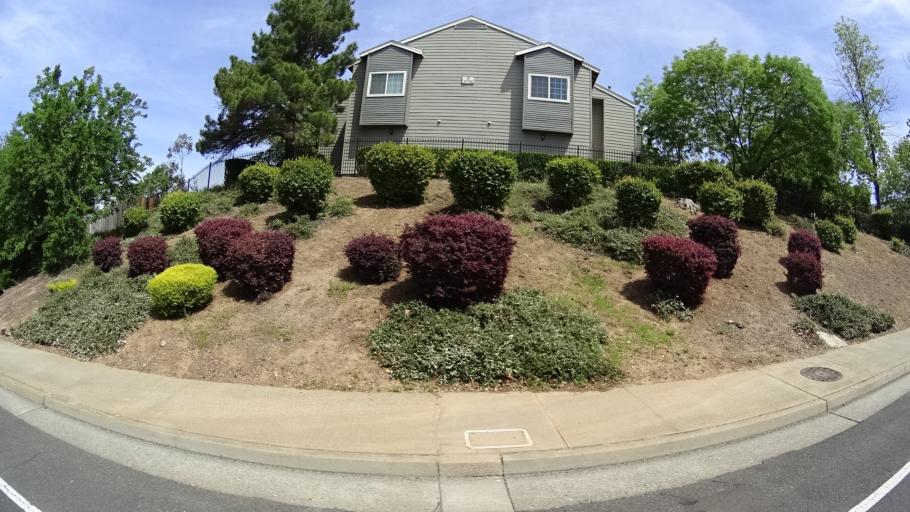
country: US
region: California
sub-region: Placer County
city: Rocklin
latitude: 38.7913
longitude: -121.2593
